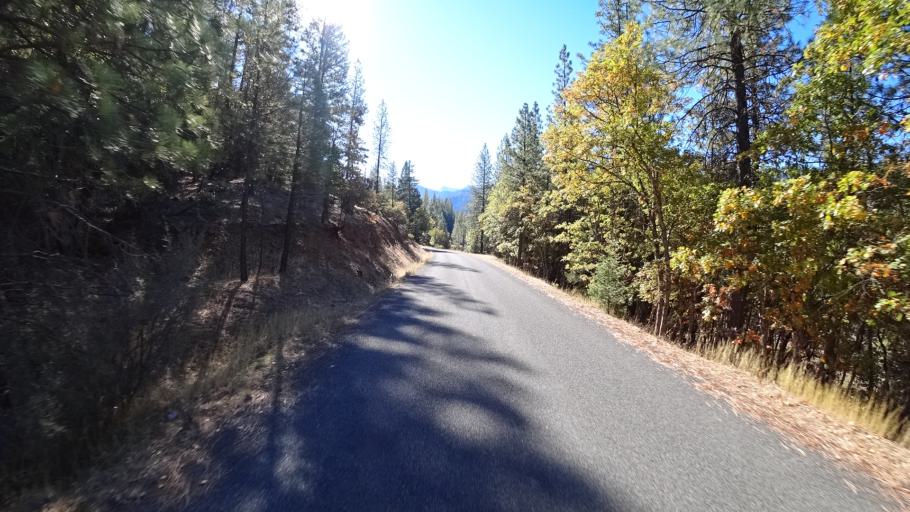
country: US
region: California
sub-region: Trinity County
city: Weaverville
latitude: 41.1280
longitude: -123.0948
